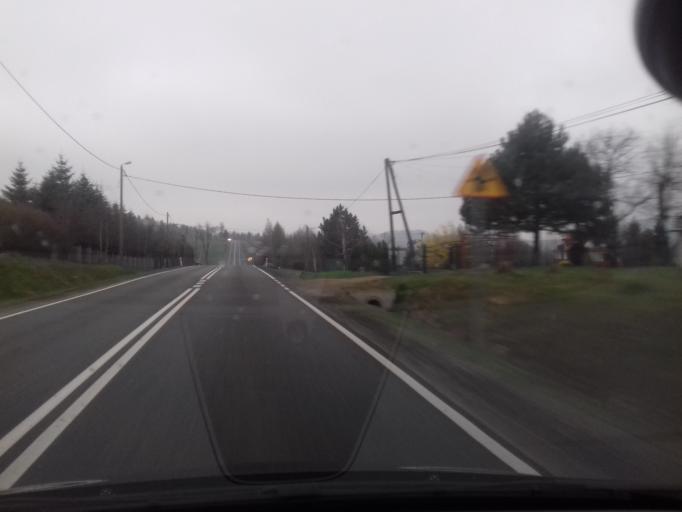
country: PL
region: Lesser Poland Voivodeship
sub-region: Powiat limanowski
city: Tymbark
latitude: 49.7220
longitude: 20.3212
